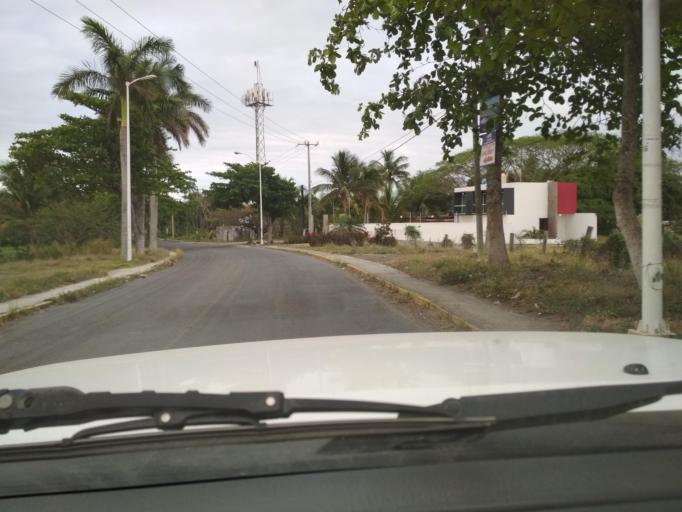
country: MX
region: Veracruz
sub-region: Medellin
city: Fraccionamiento Arboledas San Ramon
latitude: 19.0850
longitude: -96.1515
